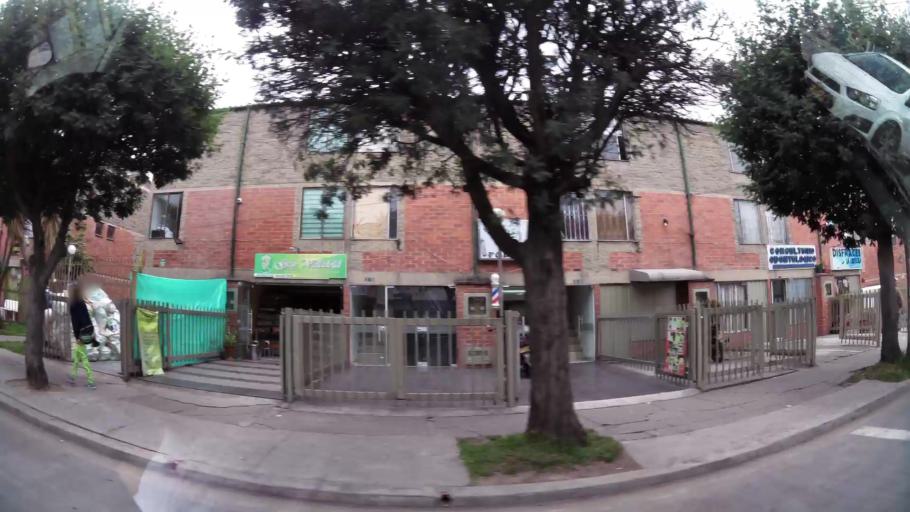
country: CO
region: Cundinamarca
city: Cota
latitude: 4.7645
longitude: -74.0366
